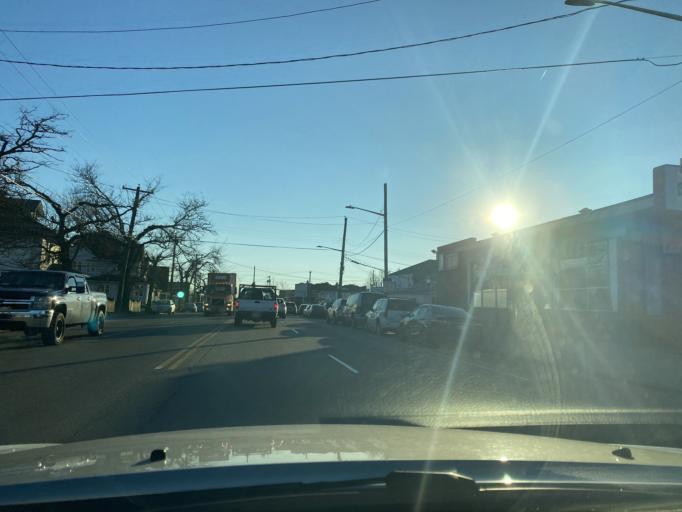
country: US
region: New York
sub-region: Nassau County
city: Inwood
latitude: 40.6163
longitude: -73.7519
